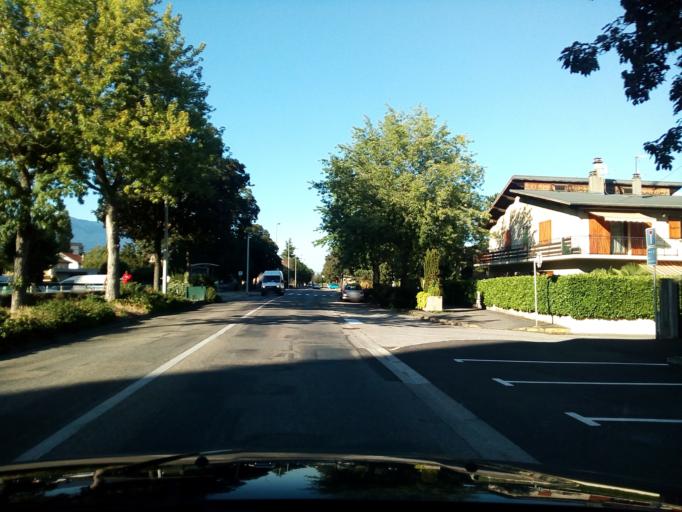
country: FR
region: Rhone-Alpes
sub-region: Departement de l'Isere
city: Echirolles
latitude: 45.1430
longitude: 5.7224
